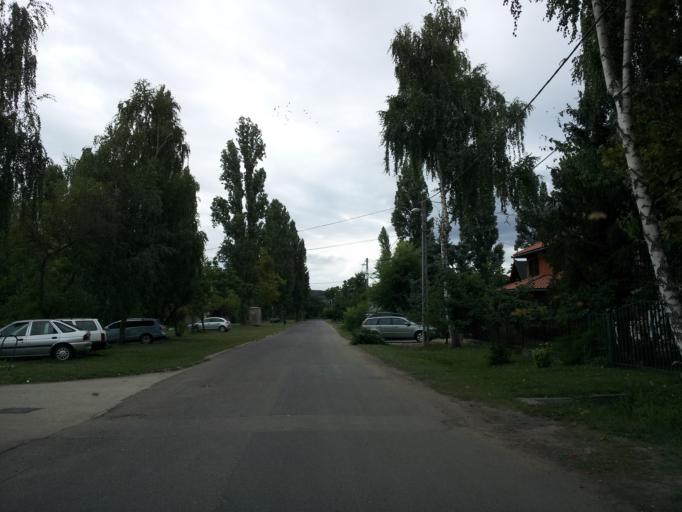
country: HU
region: Somogy
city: Zamardi
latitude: 46.8832
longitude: 17.9367
